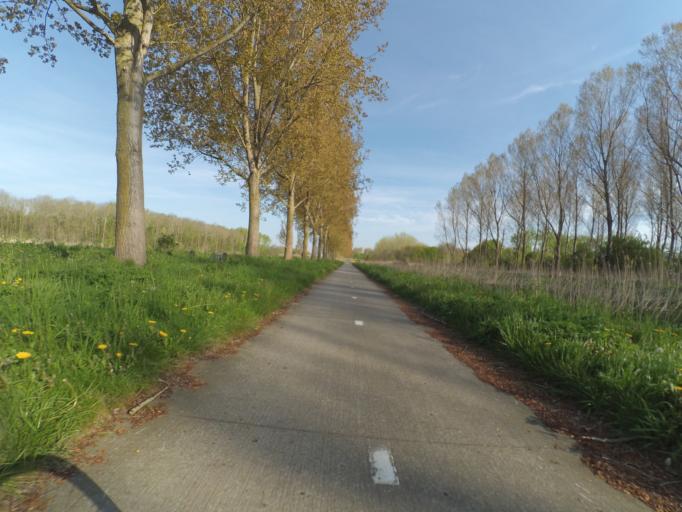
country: NL
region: North Holland
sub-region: Gemeente Huizen
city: Huizen
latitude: 52.3515
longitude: 5.2786
